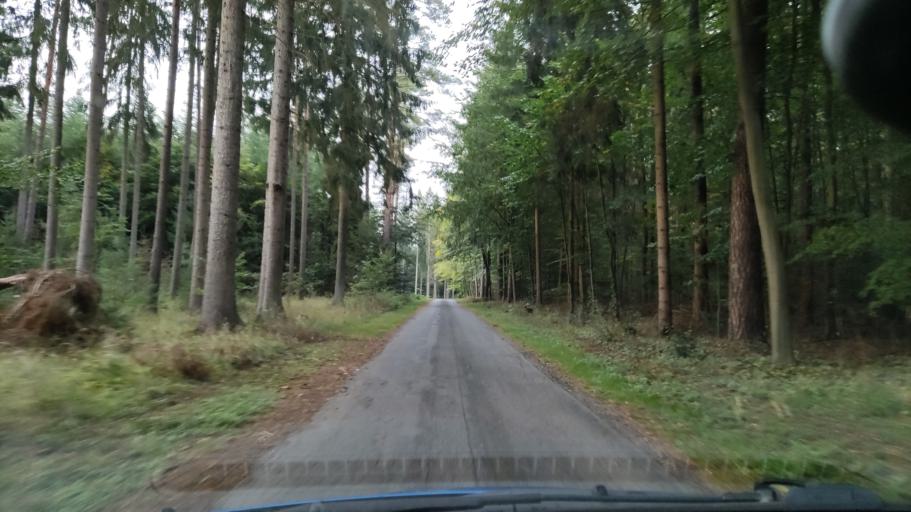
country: DE
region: Lower Saxony
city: Karwitz
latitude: 53.0831
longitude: 10.9735
